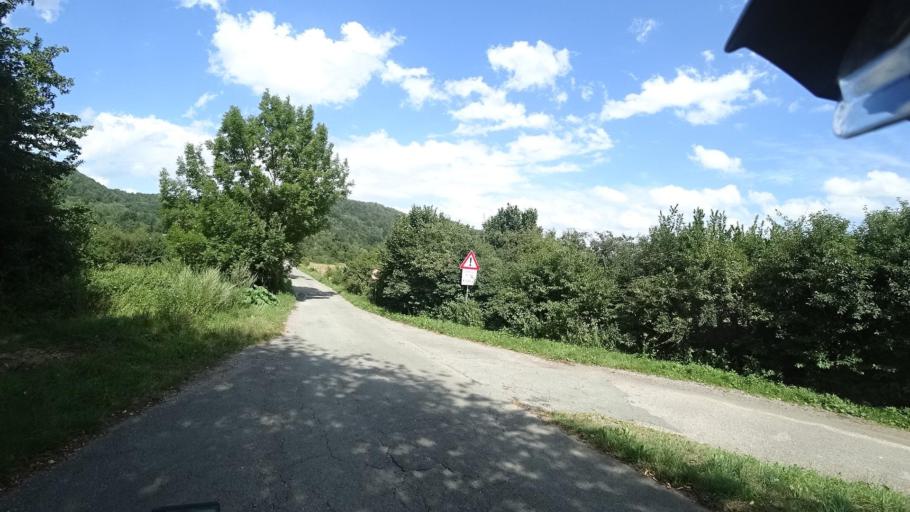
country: HR
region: Licko-Senjska
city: Brinje
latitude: 45.1452
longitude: 15.0323
